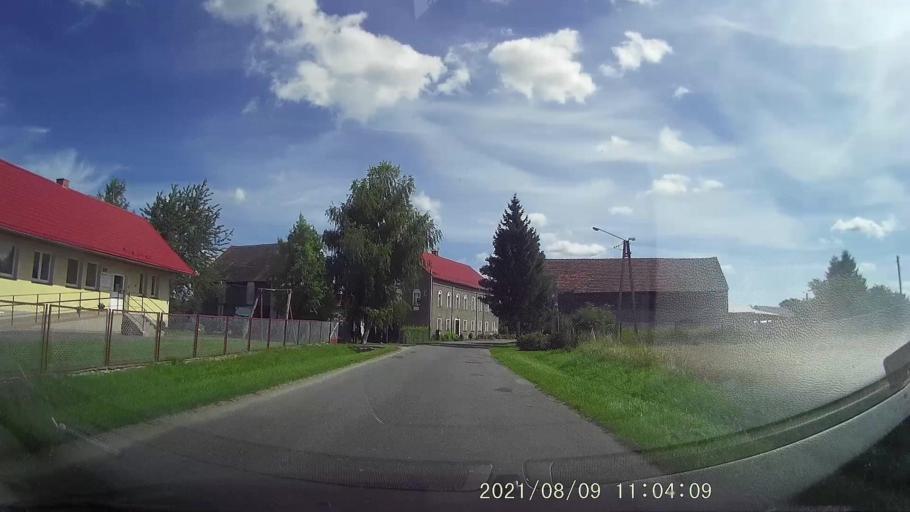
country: PL
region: Lower Silesian Voivodeship
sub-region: Powiat klodzki
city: Bozkow
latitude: 50.4636
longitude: 16.5690
